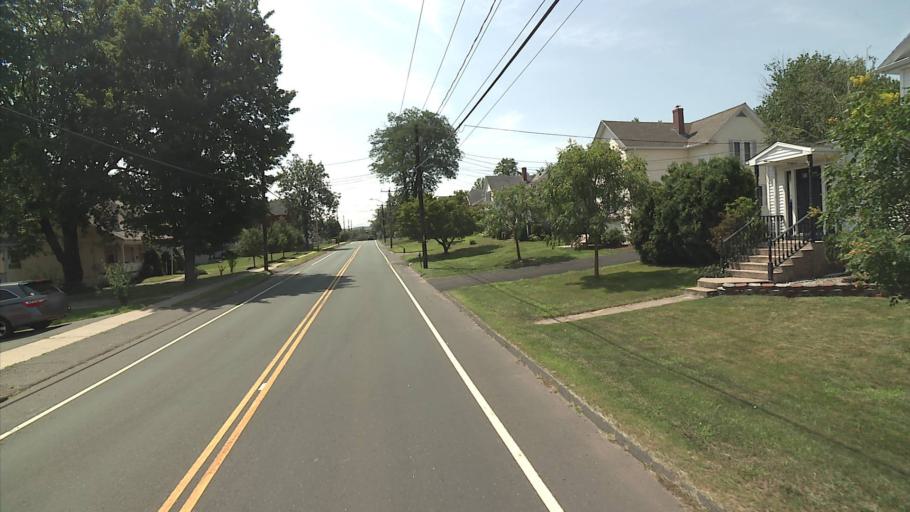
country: US
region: Connecticut
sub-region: Hartford County
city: Kensington
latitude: 41.6376
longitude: -72.7692
